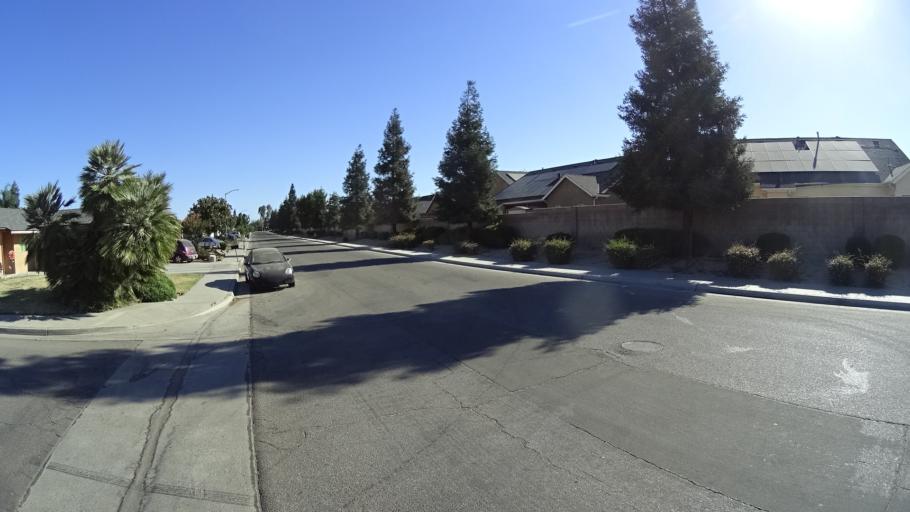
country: US
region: California
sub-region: Fresno County
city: West Park
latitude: 36.7795
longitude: -119.8670
